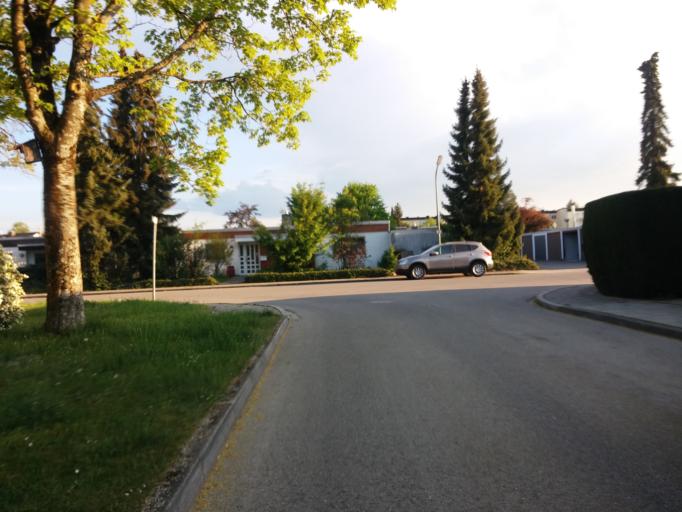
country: DE
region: Bavaria
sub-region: Upper Bavaria
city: Vaterstetten
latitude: 48.1053
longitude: 11.7908
